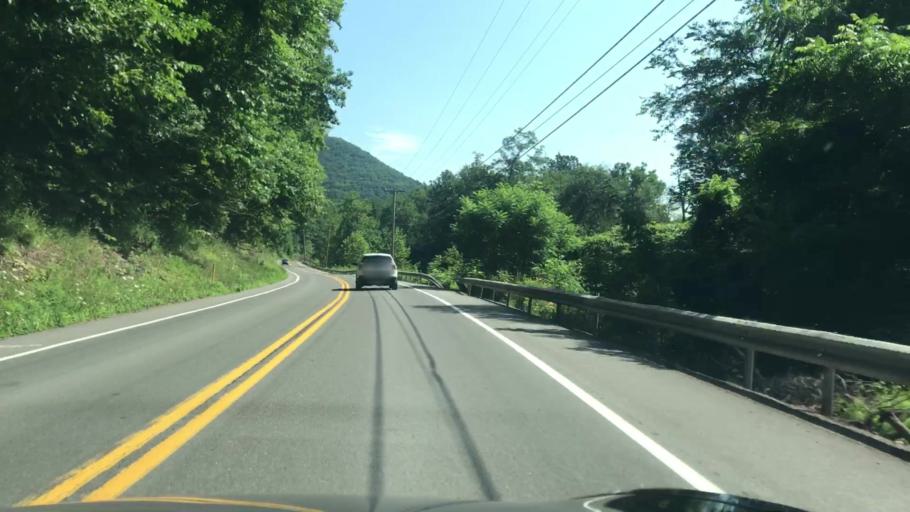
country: US
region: Pennsylvania
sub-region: Lycoming County
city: Garden View
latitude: 41.4264
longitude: -77.0123
